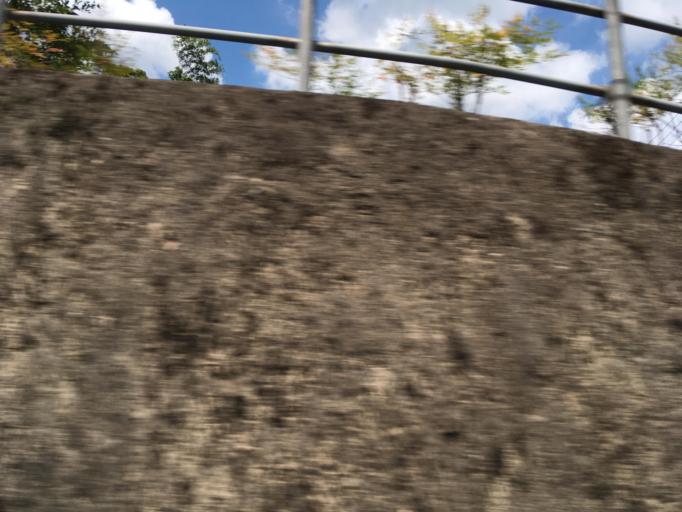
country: TW
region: Taiwan
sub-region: Yilan
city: Yilan
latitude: 24.9328
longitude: 121.6913
